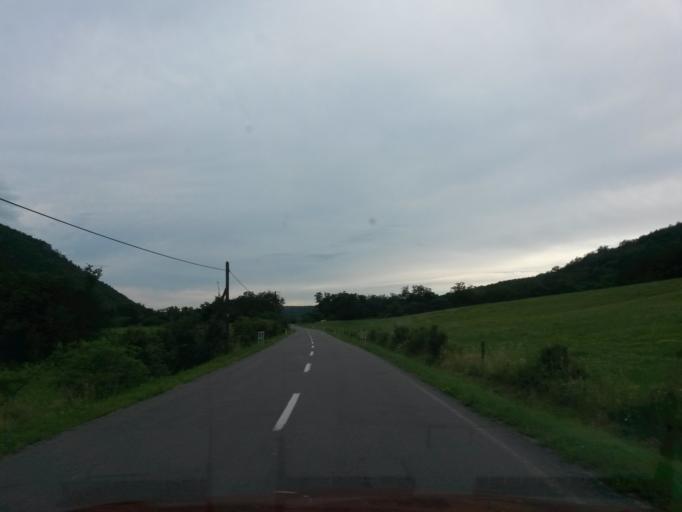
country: SK
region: Banskobystricky
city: Velky Krtis
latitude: 48.3197
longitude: 19.4052
